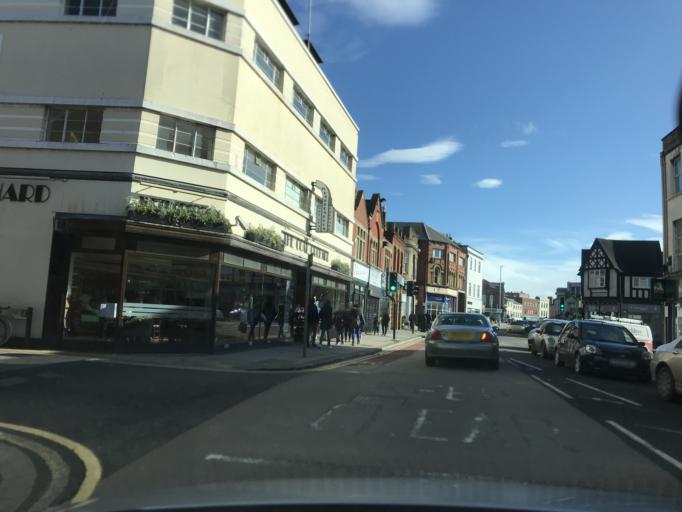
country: GB
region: England
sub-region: Somerset
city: Taunton
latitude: 51.0185
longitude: -3.1050
